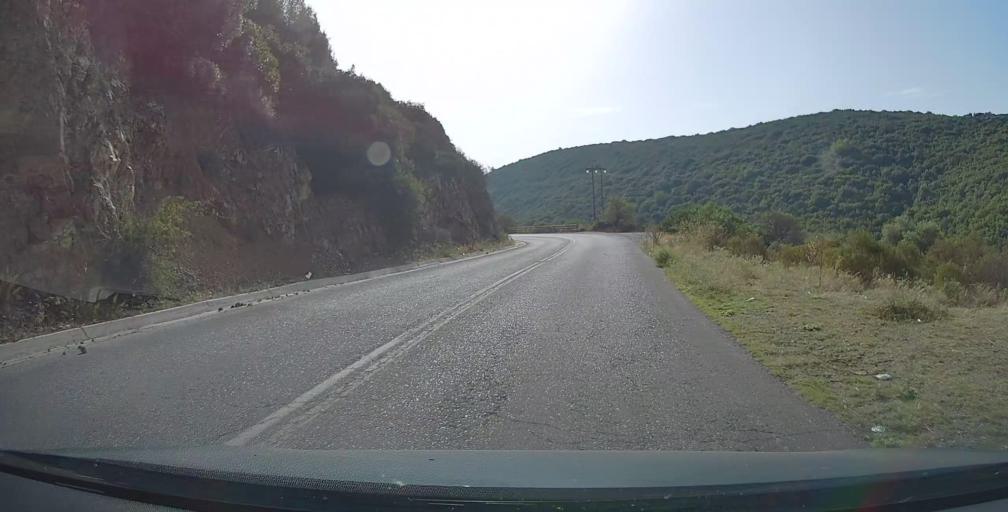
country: GR
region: Central Macedonia
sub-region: Nomos Chalkidikis
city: Sykia
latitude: 39.9628
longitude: 23.9348
